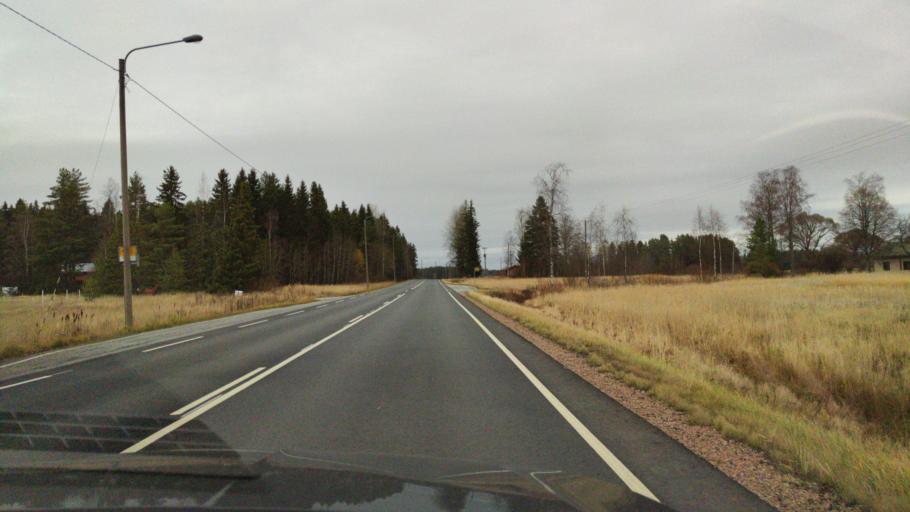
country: FI
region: Varsinais-Suomi
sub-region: Turku
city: Vahto
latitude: 60.6673
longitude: 22.4349
